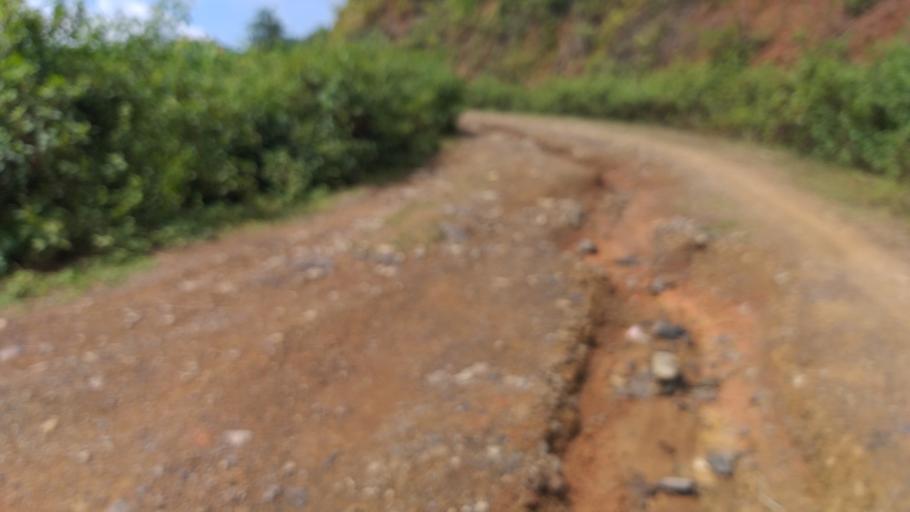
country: VN
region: Huyen Dien Bien
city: Dien Bien Phu
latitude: 21.4171
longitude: 102.6839
